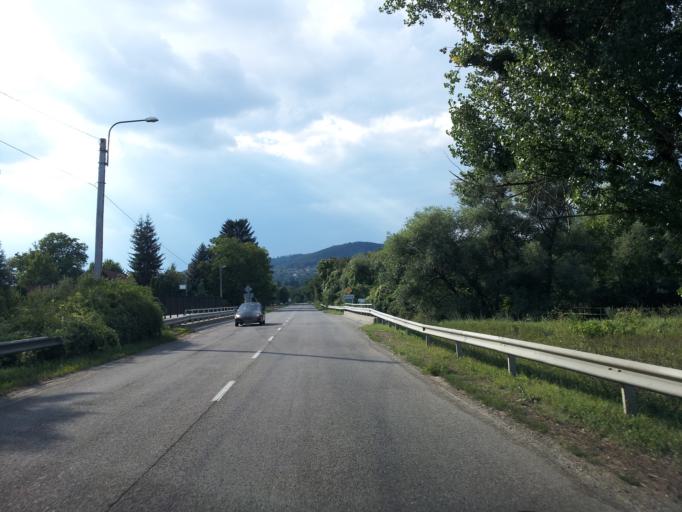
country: HU
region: Pest
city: Veroce
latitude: 47.8244
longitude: 19.0192
